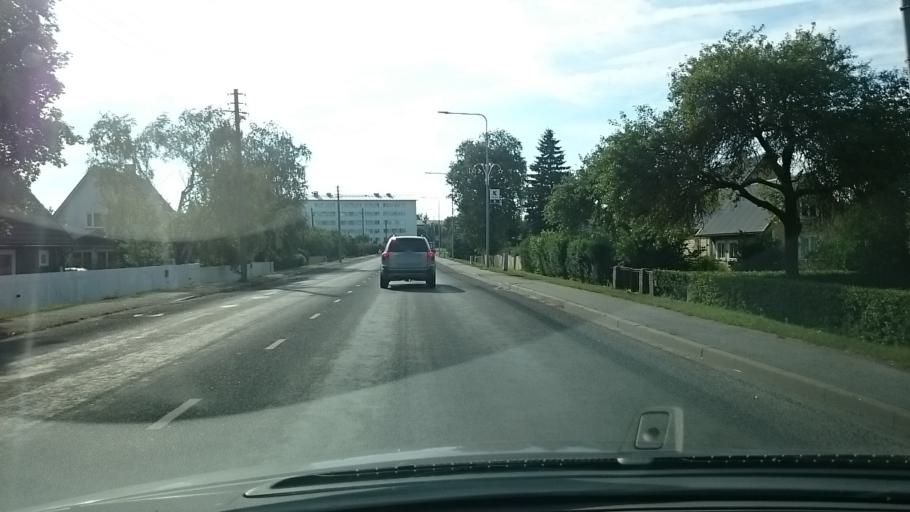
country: EE
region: Laeaene
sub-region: Haapsalu linn
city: Haapsalu
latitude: 58.9384
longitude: 23.5500
